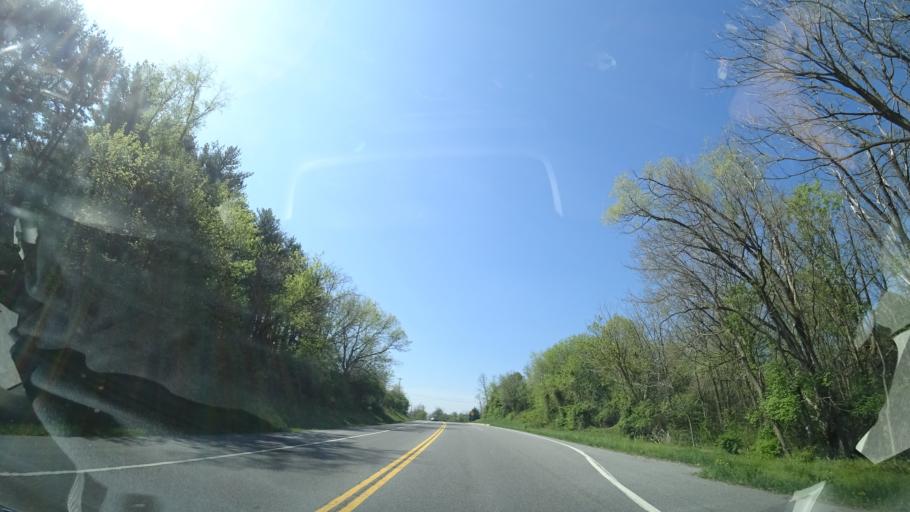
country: US
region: Maryland
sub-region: Washington County
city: Robinwood
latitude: 39.5800
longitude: -77.6444
